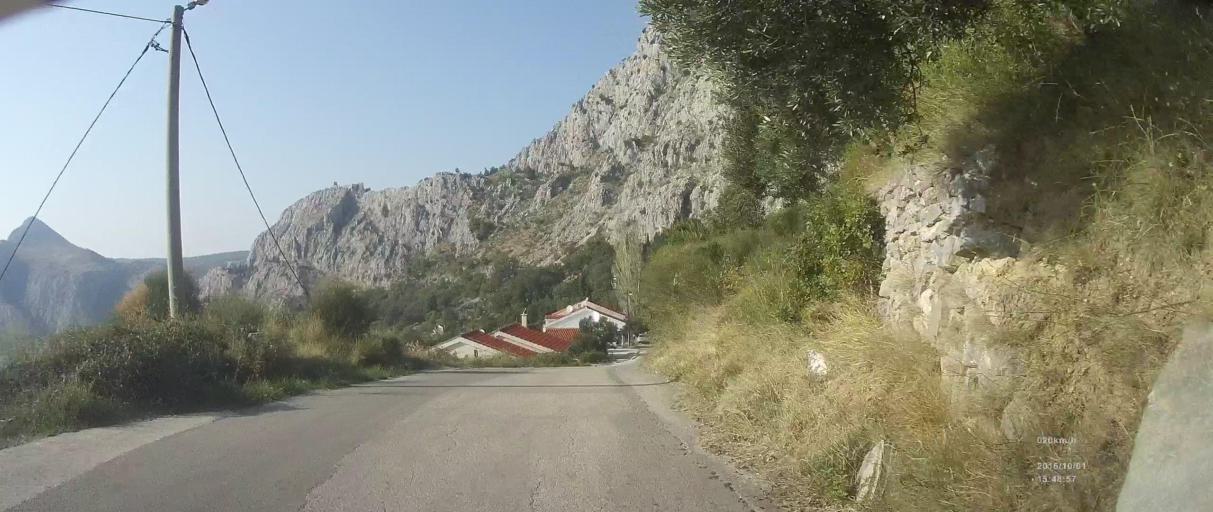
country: HR
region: Splitsko-Dalmatinska
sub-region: Grad Omis
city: Omis
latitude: 43.4385
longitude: 16.7074
